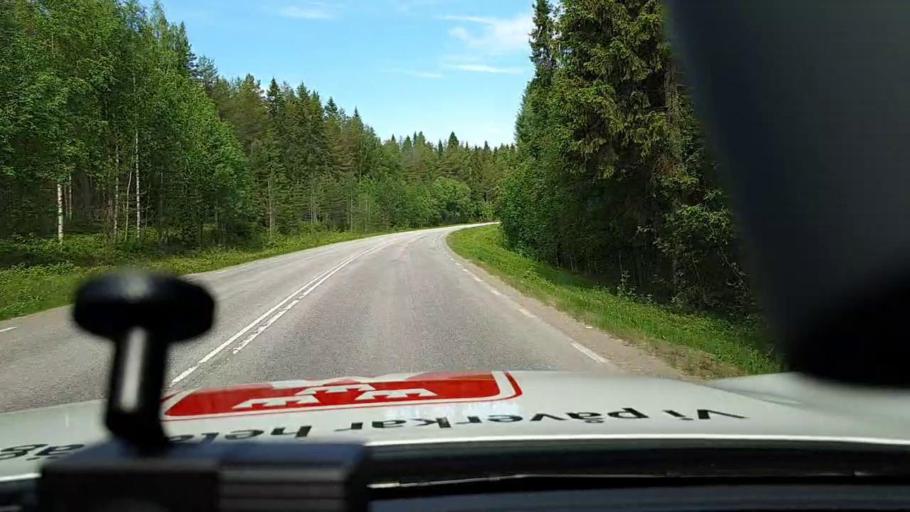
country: SE
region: Norrbotten
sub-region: Lulea Kommun
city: Gammelstad
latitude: 65.5891
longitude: 22.0034
